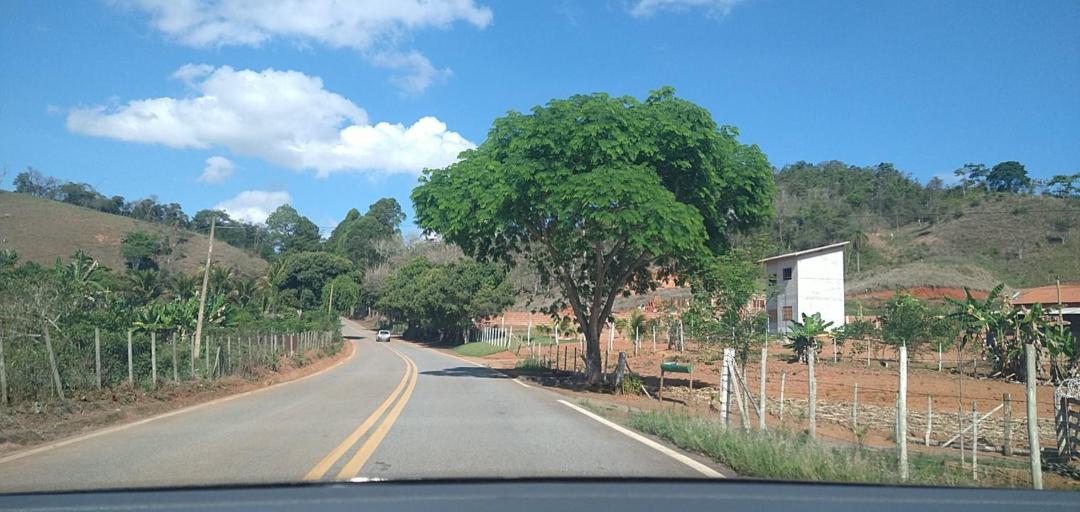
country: BR
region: Minas Gerais
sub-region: Alvinopolis
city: Alvinopolis
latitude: -20.0359
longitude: -43.0414
